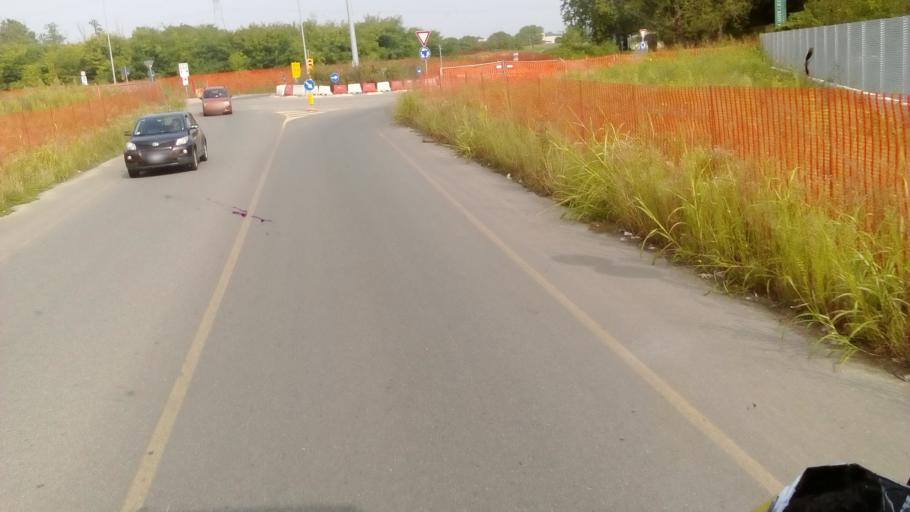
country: IT
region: Lombardy
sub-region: Provincia di Como
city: Rovellasca
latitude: 45.6793
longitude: 9.0548
